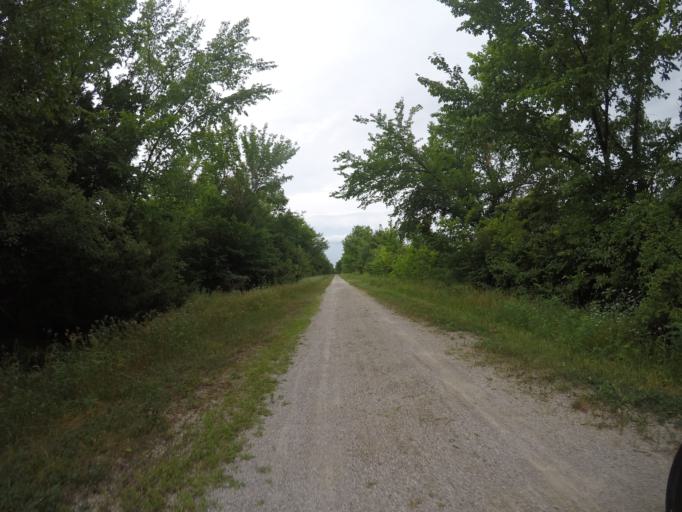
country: US
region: Kansas
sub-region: Franklin County
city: Ottawa
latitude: 38.5631
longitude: -95.2712
